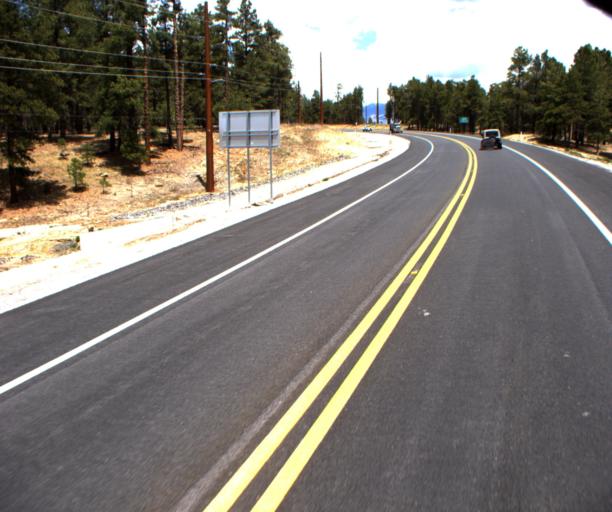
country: US
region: Arizona
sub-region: Coconino County
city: Kachina Village
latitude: 35.1345
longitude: -111.6863
